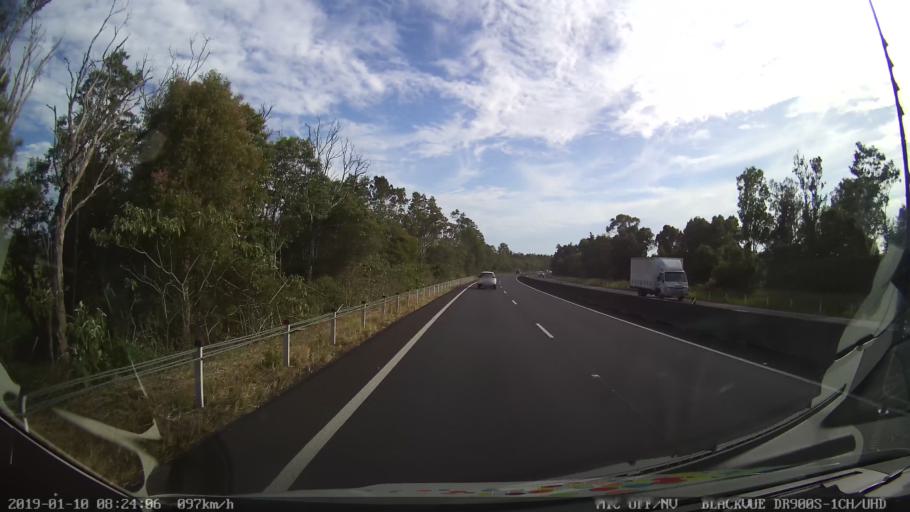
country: AU
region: New South Wales
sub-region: Coffs Harbour
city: Bonville
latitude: -30.4498
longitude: 153.0043
